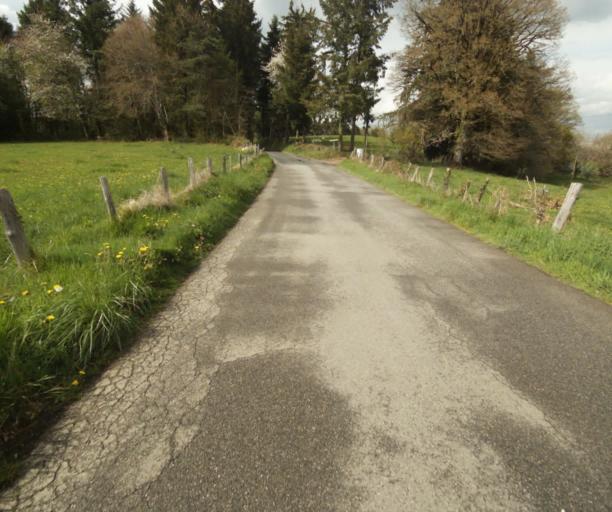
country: FR
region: Limousin
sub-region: Departement de la Correze
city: Tulle
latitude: 45.2858
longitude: 1.7448
